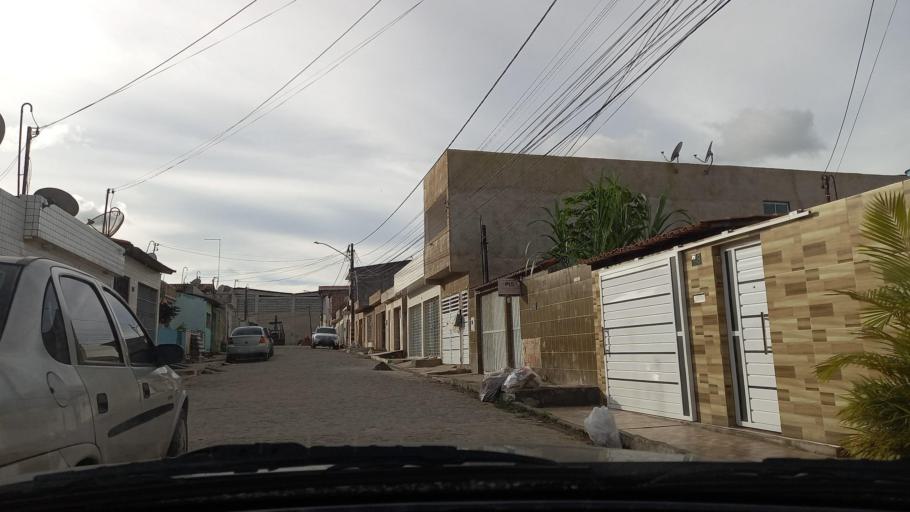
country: BR
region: Pernambuco
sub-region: Gravata
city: Gravata
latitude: -8.2009
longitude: -35.5605
